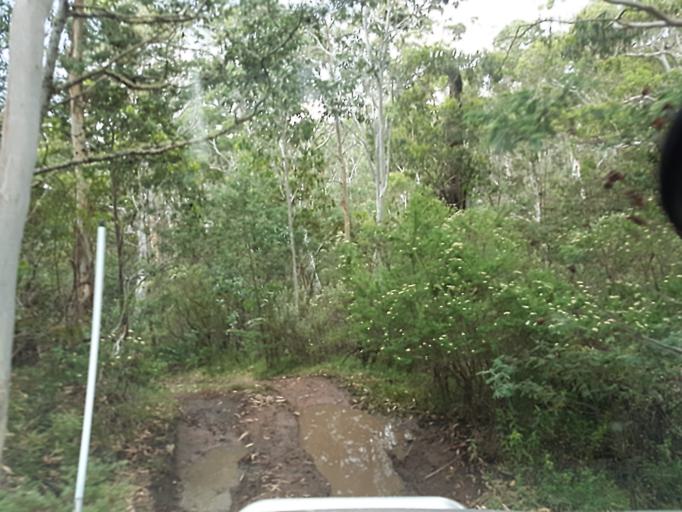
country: AU
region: New South Wales
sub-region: Snowy River
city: Jindabyne
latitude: -36.8747
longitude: 148.1726
